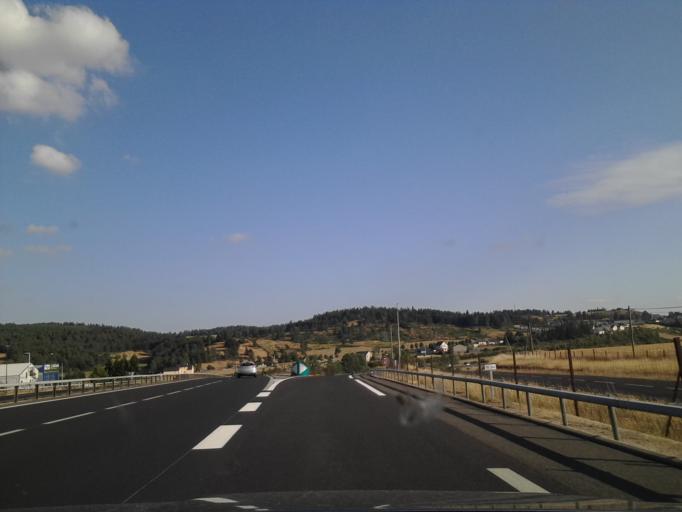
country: FR
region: Languedoc-Roussillon
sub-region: Departement de la Lozere
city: Aumont-Aubrac
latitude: 44.7354
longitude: 3.2894
